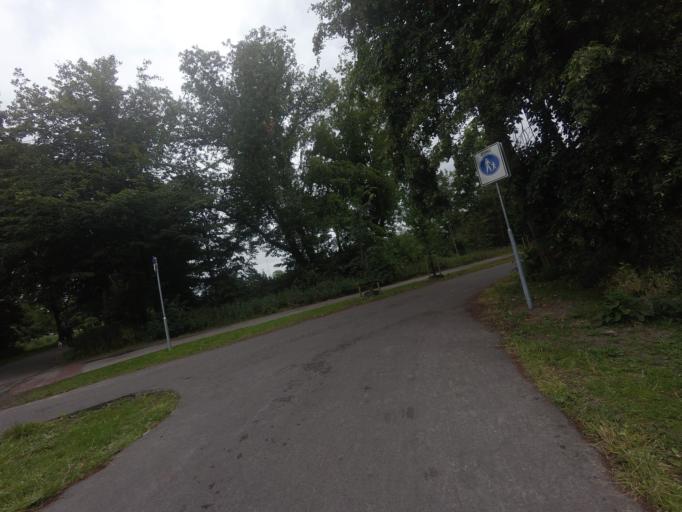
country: NL
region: North Holland
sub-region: Gemeente Bloemendaal
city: Bloemendaal
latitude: 52.4128
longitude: 4.6460
